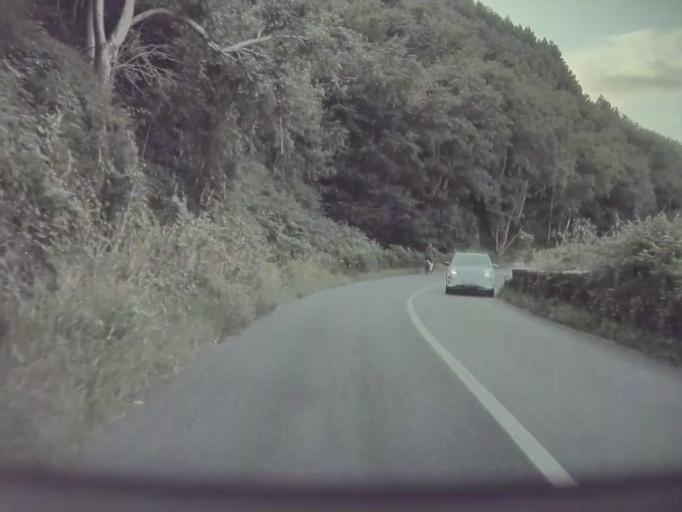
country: IE
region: Leinster
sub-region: Wicklow
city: Enniskerry
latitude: 53.2151
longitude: -6.1786
